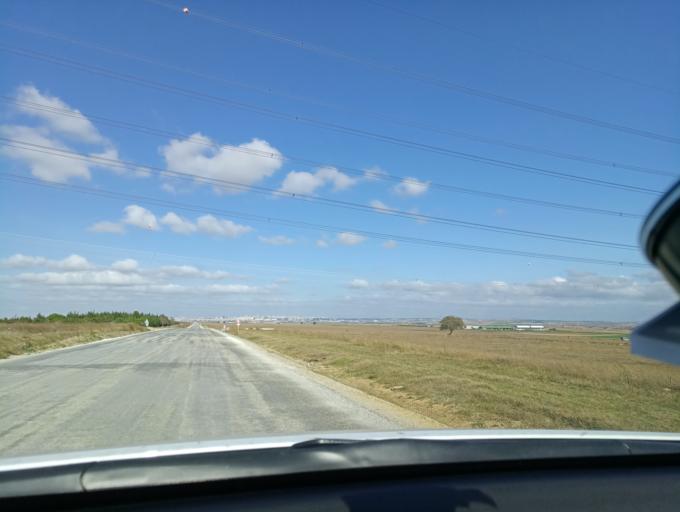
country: TR
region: Tekirdag
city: Corlu
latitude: 41.0601
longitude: 27.8345
